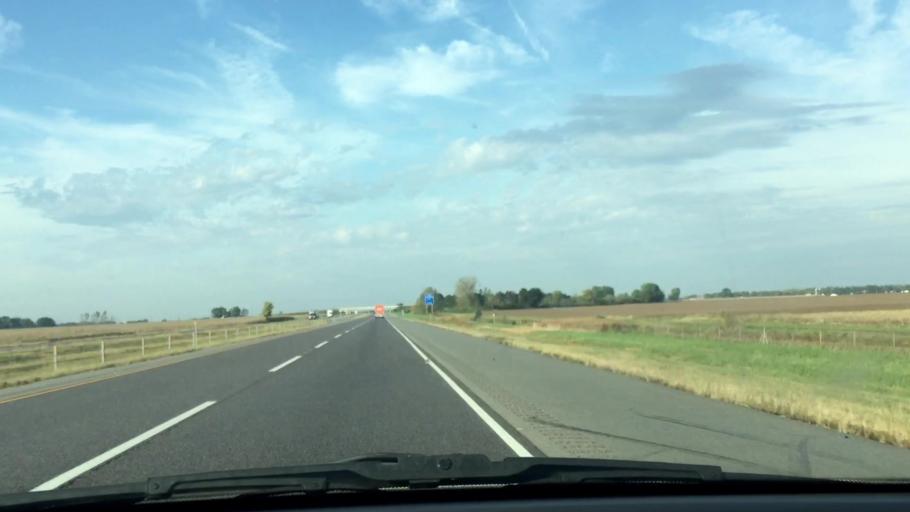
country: US
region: Illinois
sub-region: Lee County
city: Franklin Grove
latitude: 41.8390
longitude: -89.2635
